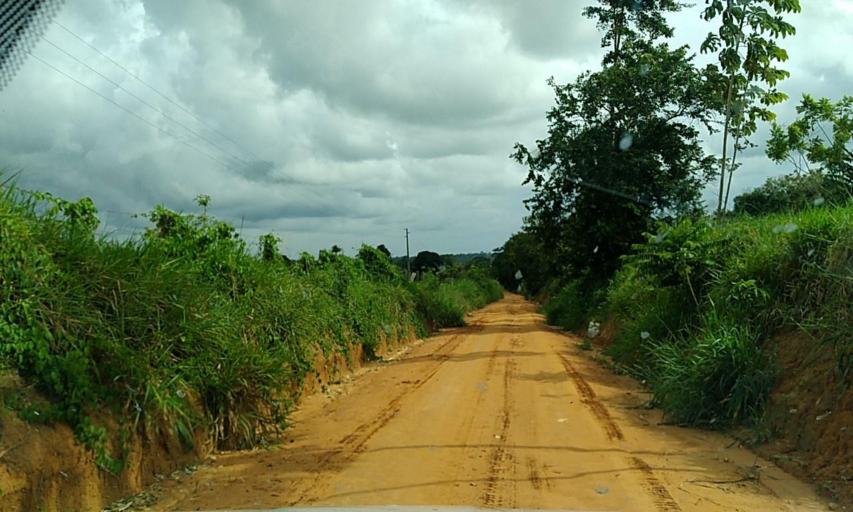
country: BR
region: Para
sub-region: Altamira
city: Altamira
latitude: -3.2996
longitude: -52.6876
